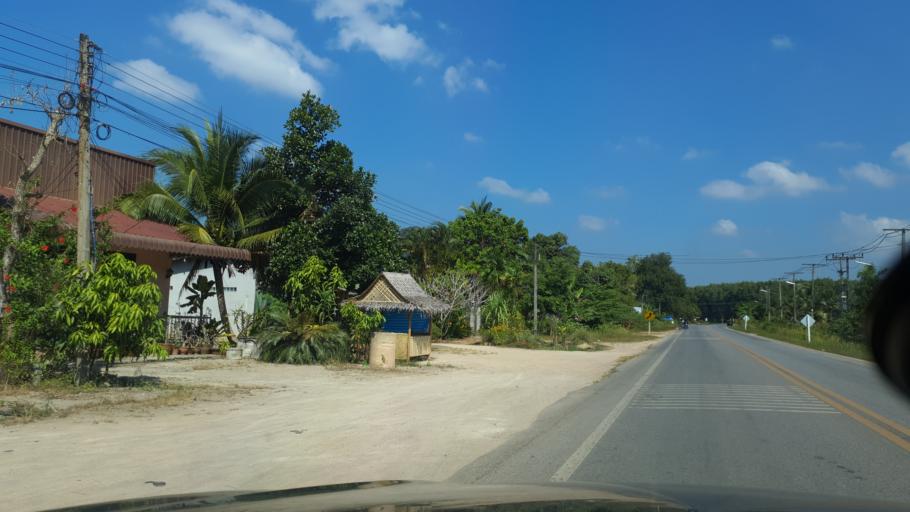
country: TH
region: Phangnga
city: Ban Ao Nang
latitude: 8.0611
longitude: 98.8593
